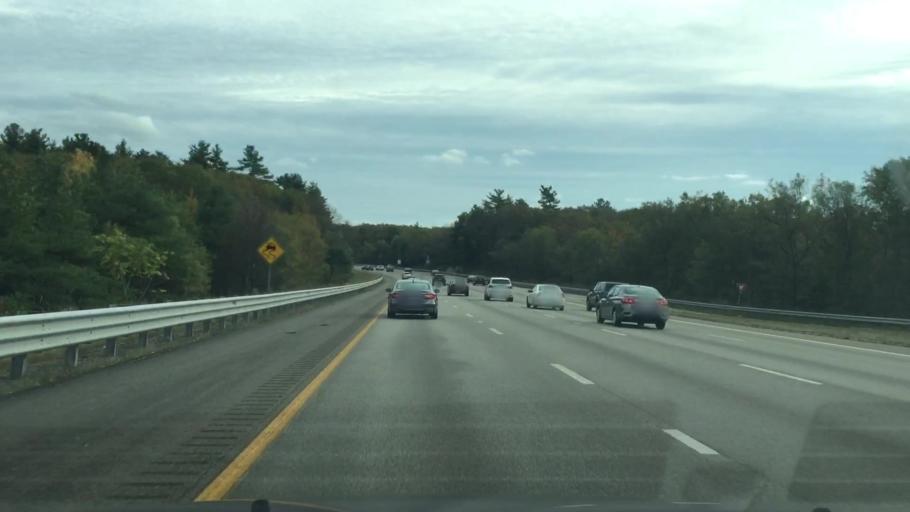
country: US
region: Massachusetts
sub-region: Norfolk County
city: Westwood
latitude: 42.2459
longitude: -71.2075
